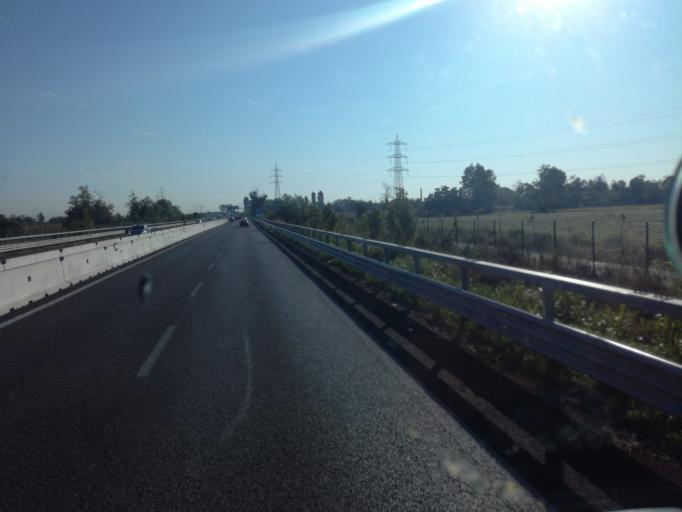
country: IT
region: Lombardy
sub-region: Citta metropolitana di Milano
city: Sant'Agata Martesana
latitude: 45.5079
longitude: 9.3987
